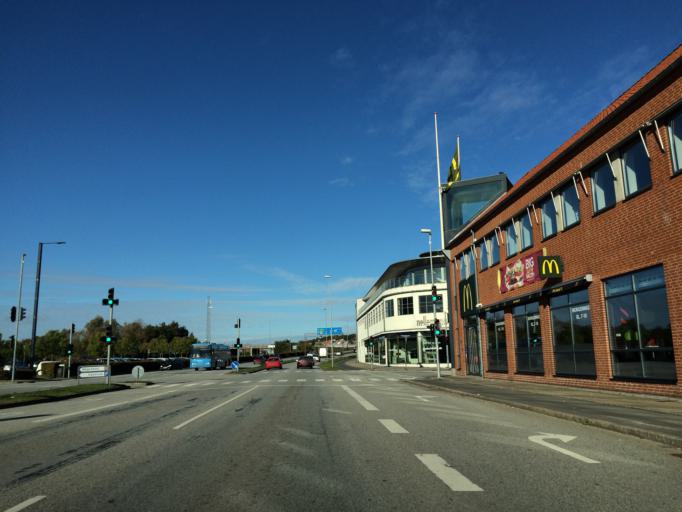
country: DK
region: Central Jutland
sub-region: Randers Kommune
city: Randers
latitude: 56.4576
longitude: 10.0334
